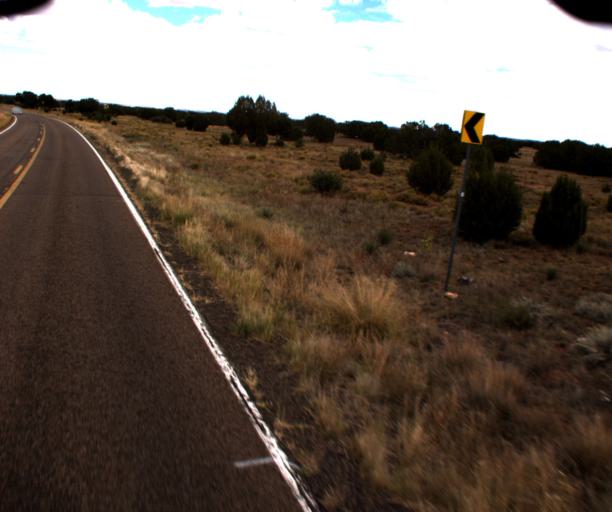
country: US
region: Arizona
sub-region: Navajo County
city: Heber-Overgaard
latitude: 34.5240
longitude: -110.4295
